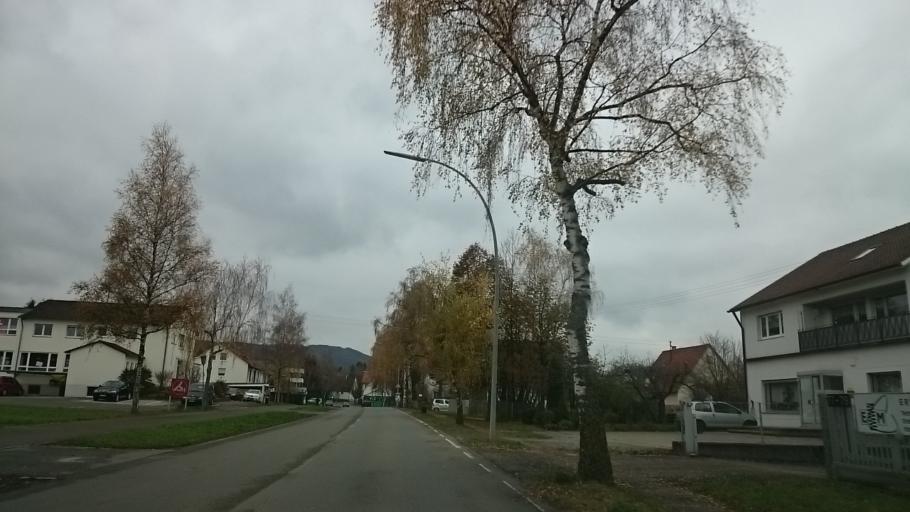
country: DE
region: Baden-Wuerttemberg
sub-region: Tuebingen Region
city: Mossingen
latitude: 48.3980
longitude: 9.0384
